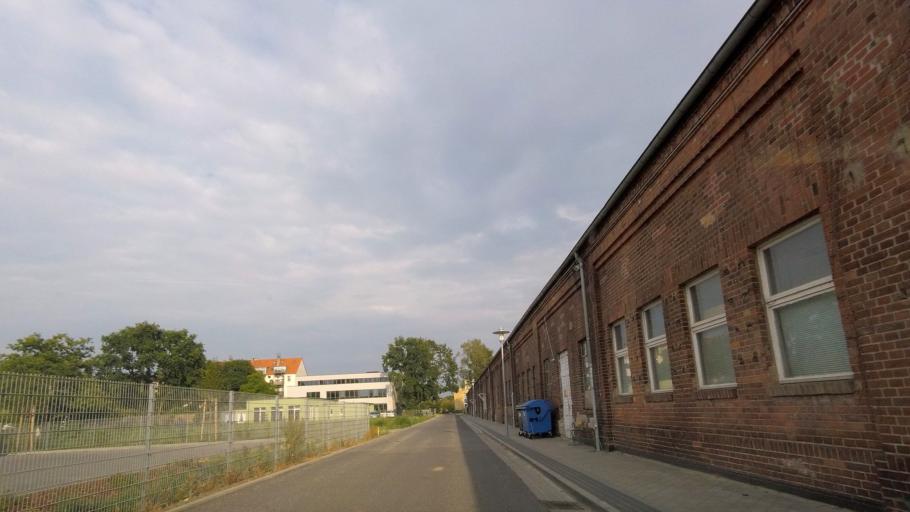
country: DE
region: Brandenburg
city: Potsdam
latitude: 52.3834
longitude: 13.1139
